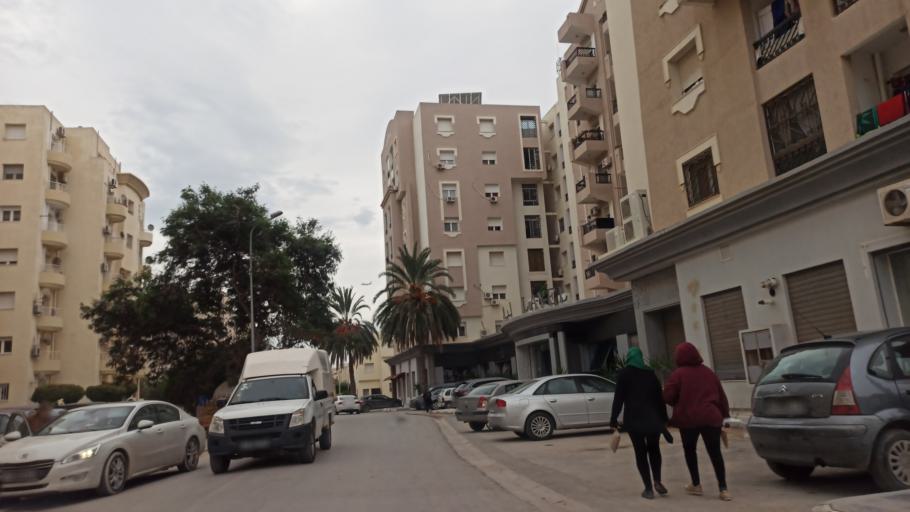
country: TN
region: Tunis
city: La Goulette
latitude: 36.8570
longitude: 10.2671
